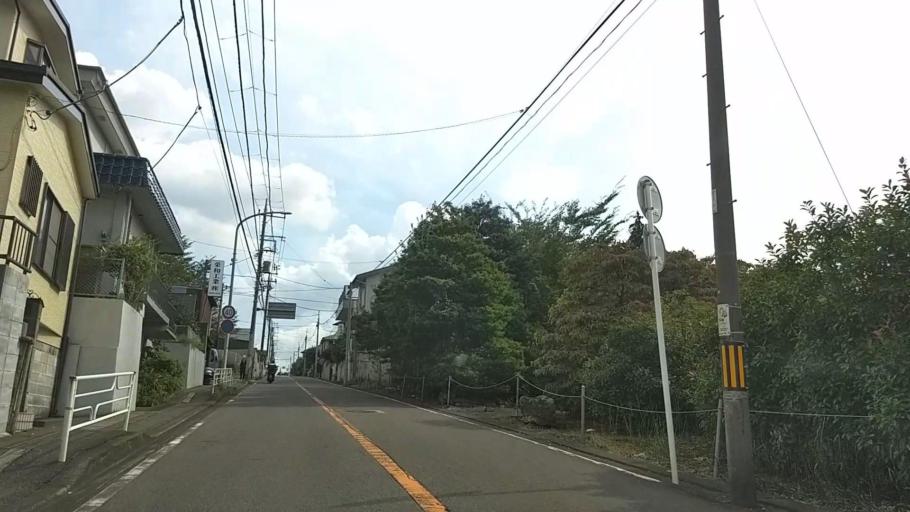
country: JP
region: Kanagawa
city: Yokohama
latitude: 35.4994
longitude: 139.5826
